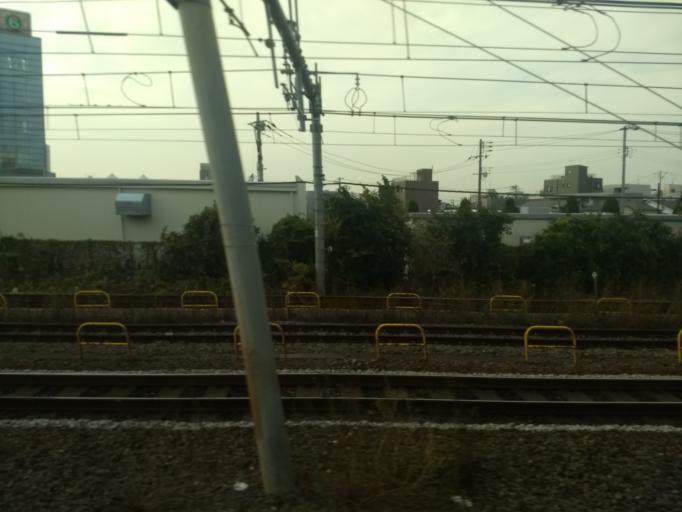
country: JP
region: Kanagawa
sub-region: Kawasaki-shi
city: Kawasaki
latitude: 35.5656
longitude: 139.7173
